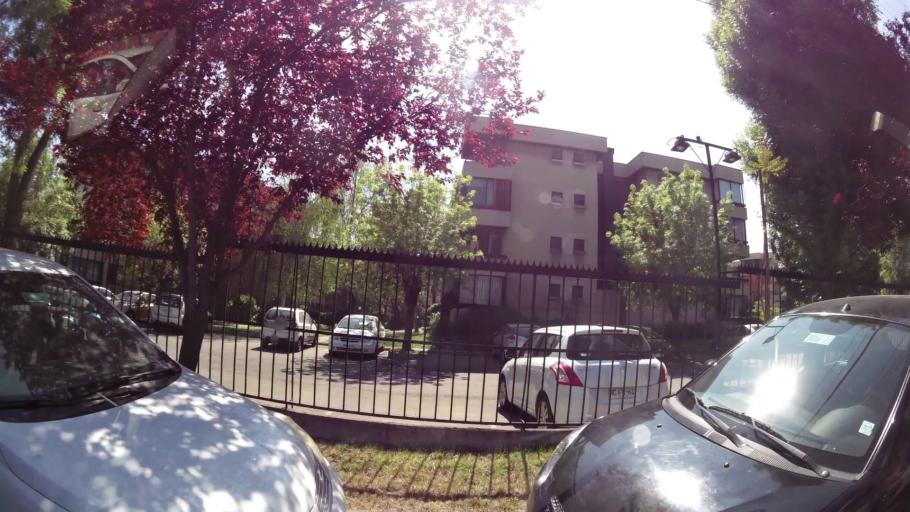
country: CL
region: Santiago Metropolitan
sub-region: Provincia de Santiago
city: Villa Presidente Frei, Nunoa, Santiago, Chile
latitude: -33.4277
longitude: -70.5445
